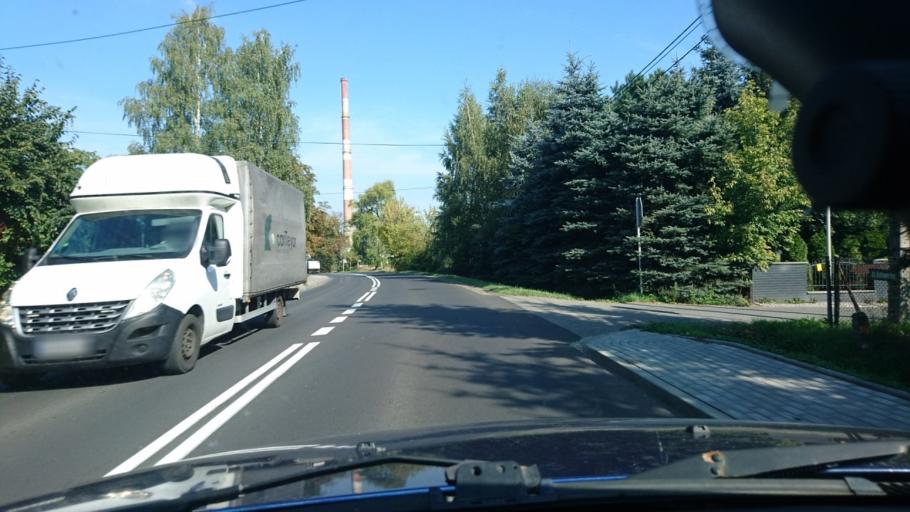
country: PL
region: Silesian Voivodeship
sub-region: Powiat bielski
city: Bestwina
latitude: 49.8666
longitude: 19.0300
